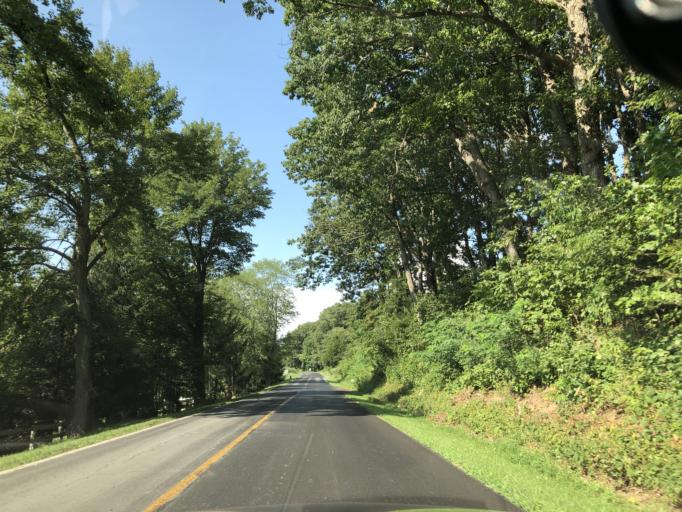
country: US
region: Maryland
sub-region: Frederick County
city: Linganore
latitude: 39.4413
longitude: -77.1778
